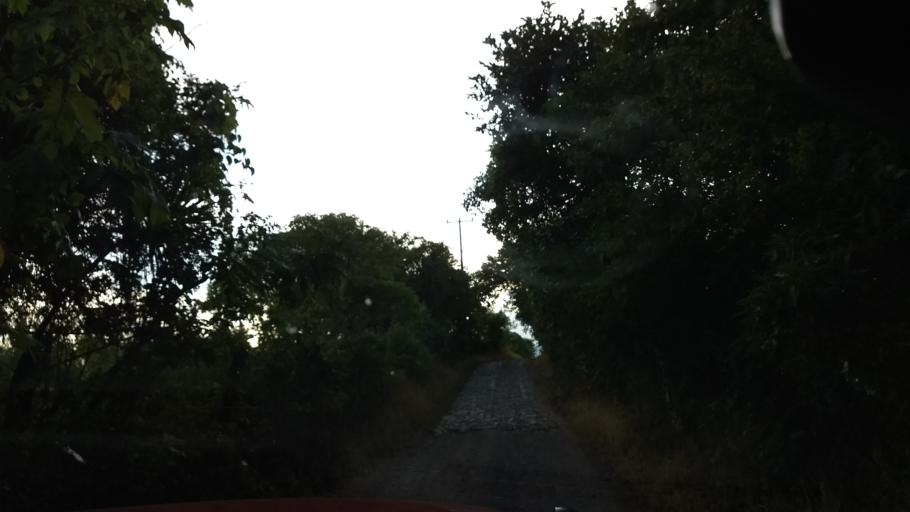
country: MX
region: Jalisco
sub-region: San Gabriel
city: Alista
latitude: 19.5069
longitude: -103.7550
